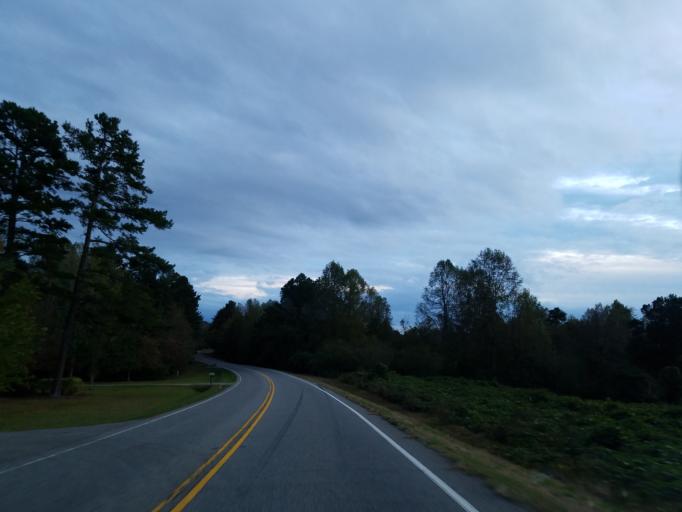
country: US
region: Georgia
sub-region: Dawson County
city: Dawsonville
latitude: 34.3895
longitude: -84.1265
